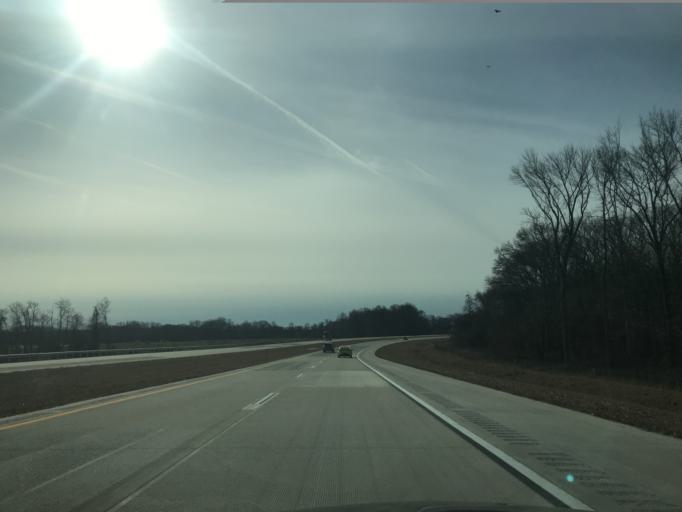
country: US
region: Delaware
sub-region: New Castle County
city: Middletown
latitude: 39.5037
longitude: -75.6941
